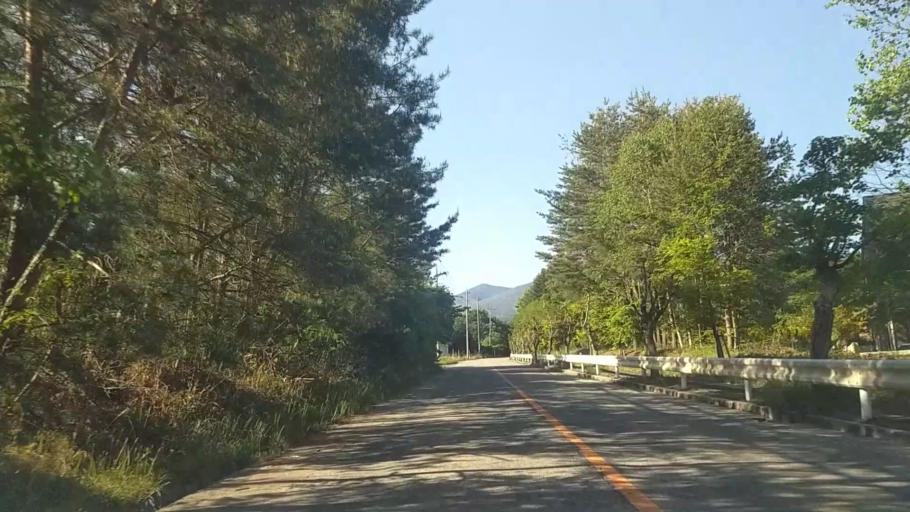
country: JP
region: Nagano
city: Chino
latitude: 35.8839
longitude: 138.3187
